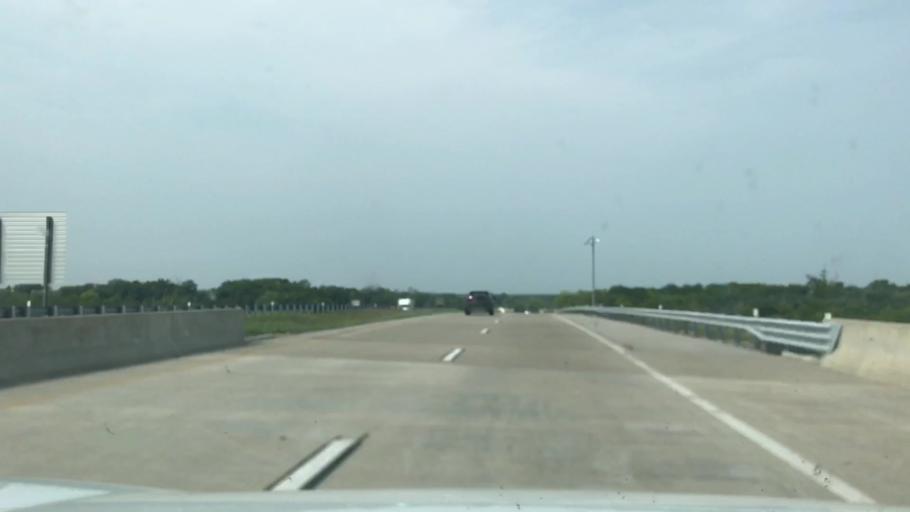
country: US
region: Missouri
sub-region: Saint Charles County
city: Cottleville
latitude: 38.7336
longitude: -90.6505
